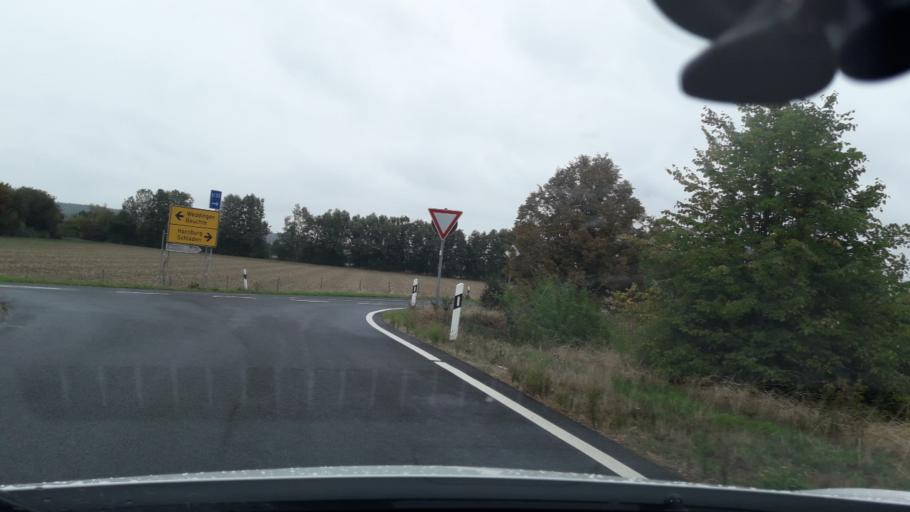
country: DE
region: Lower Saxony
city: Schladen
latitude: 52.0066
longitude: 10.5442
